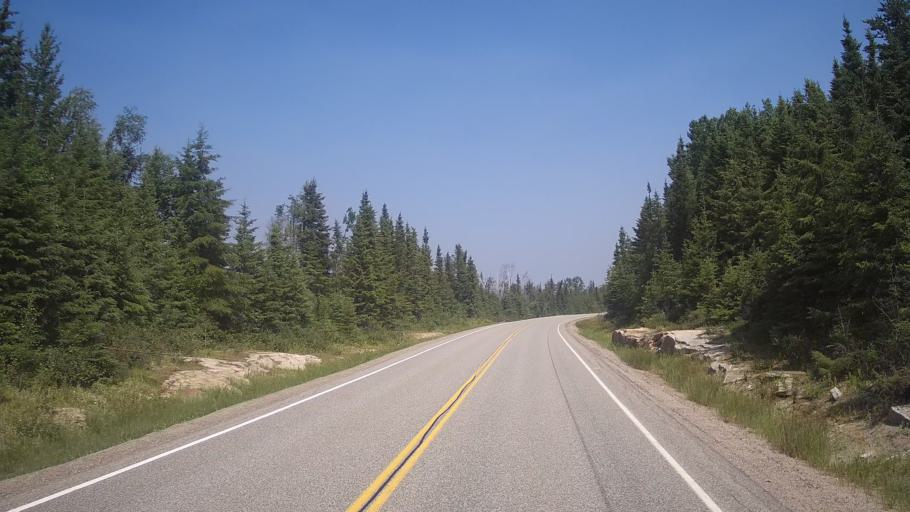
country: CA
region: Ontario
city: Timmins
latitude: 48.0445
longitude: -81.5838
